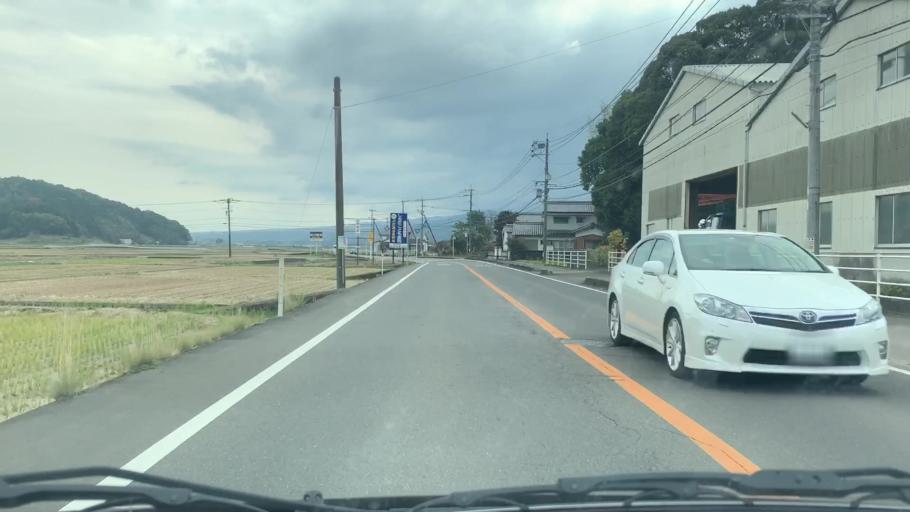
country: JP
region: Saga Prefecture
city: Kashima
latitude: 33.1458
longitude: 130.0631
